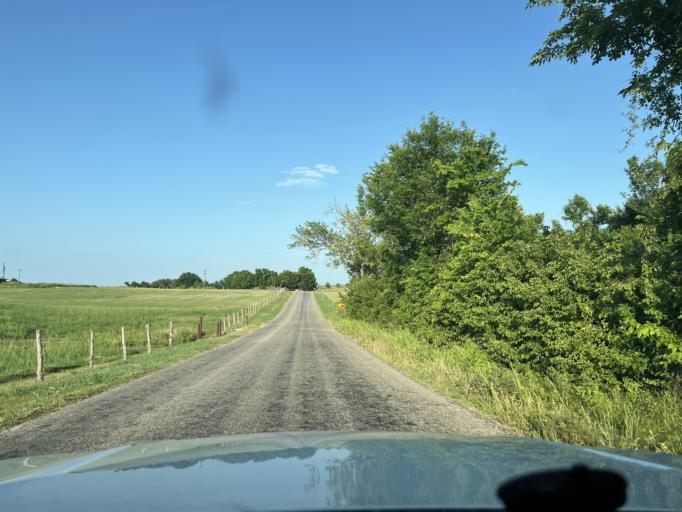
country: US
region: Texas
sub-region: Washington County
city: Brenham
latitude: 30.2298
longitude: -96.3823
